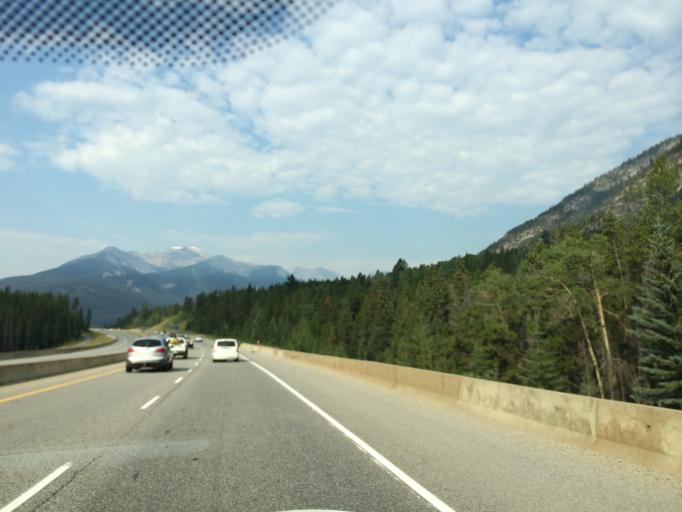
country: CA
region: Alberta
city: Banff
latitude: 51.1754
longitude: -115.6443
